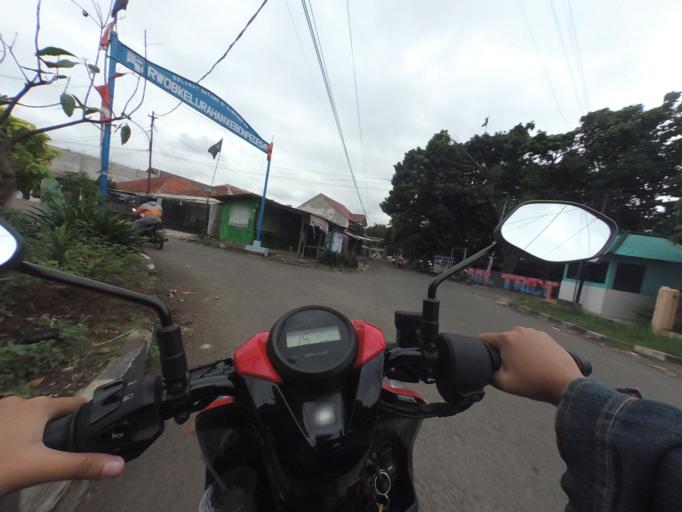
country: ID
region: West Java
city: Bogor
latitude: -6.5697
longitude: 106.7959
